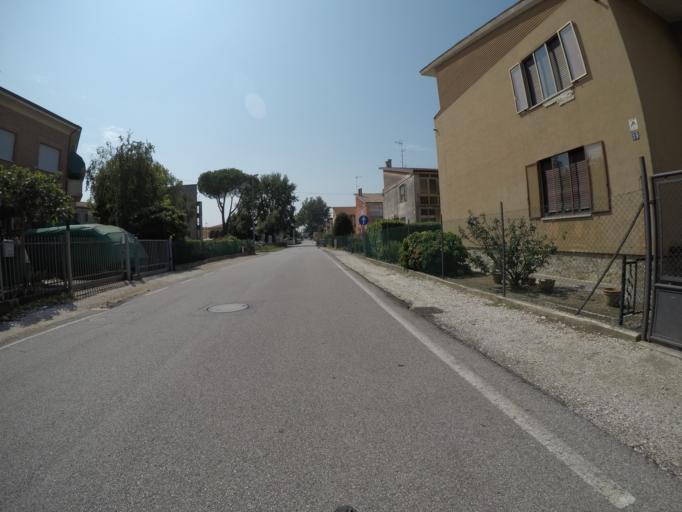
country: IT
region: Veneto
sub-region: Provincia di Rovigo
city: Lendinara
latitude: 45.0880
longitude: 11.5898
